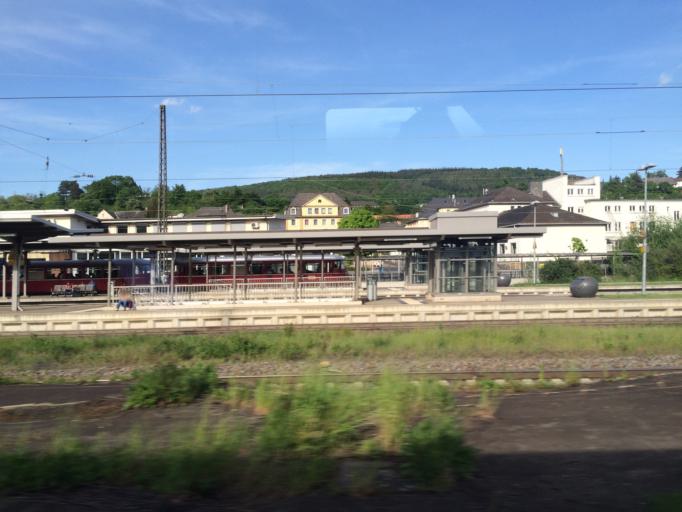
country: DE
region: Rheinland-Pfalz
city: Lahnstein
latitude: 50.3162
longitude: 7.5991
